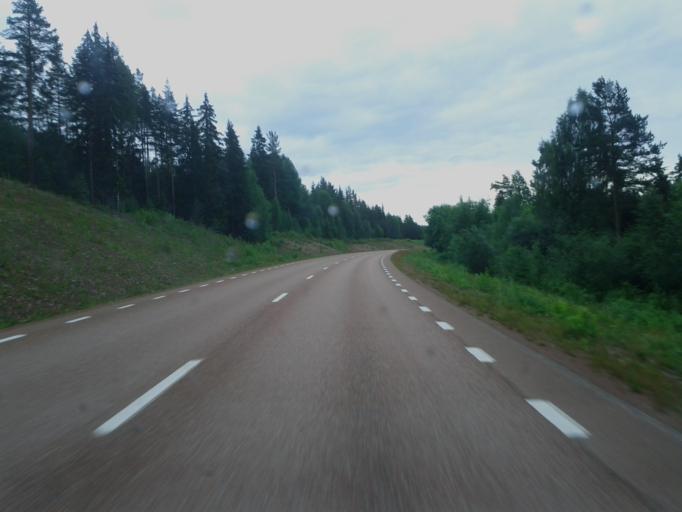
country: SE
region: Dalarna
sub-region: Alvdalens Kommun
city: AElvdalen
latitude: 61.2804
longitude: 13.9529
